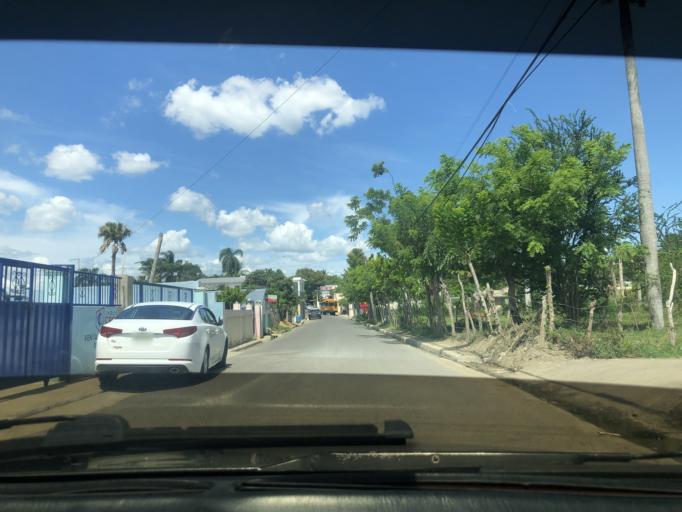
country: DO
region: Santiago
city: Santiago de los Caballeros
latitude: 19.3987
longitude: -70.6661
